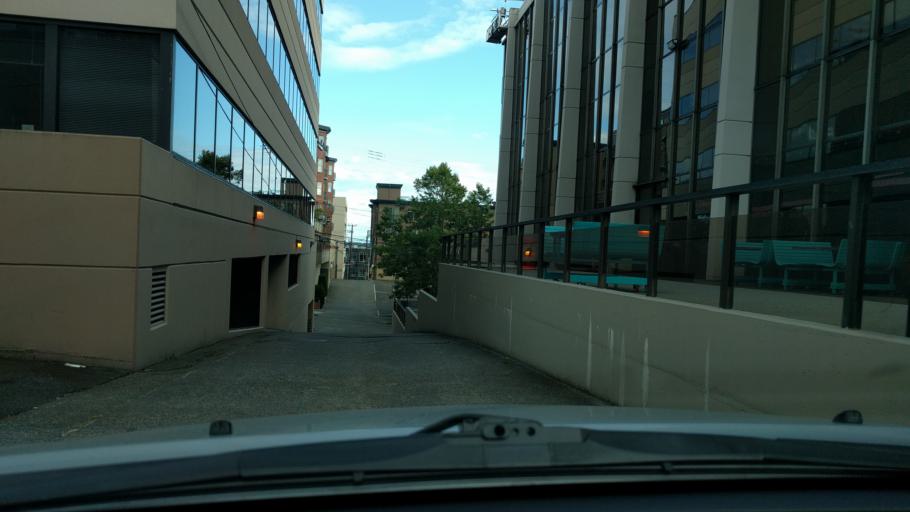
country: US
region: Washington
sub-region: King County
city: Seattle
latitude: 47.6203
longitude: -122.3574
